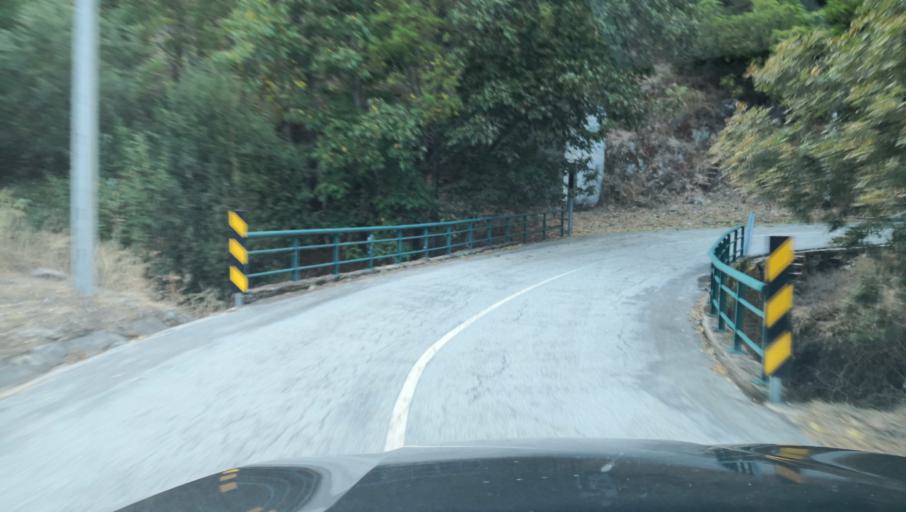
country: PT
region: Vila Real
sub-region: Santa Marta de Penaguiao
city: Santa Marta de Penaguiao
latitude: 41.2434
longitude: -7.8560
